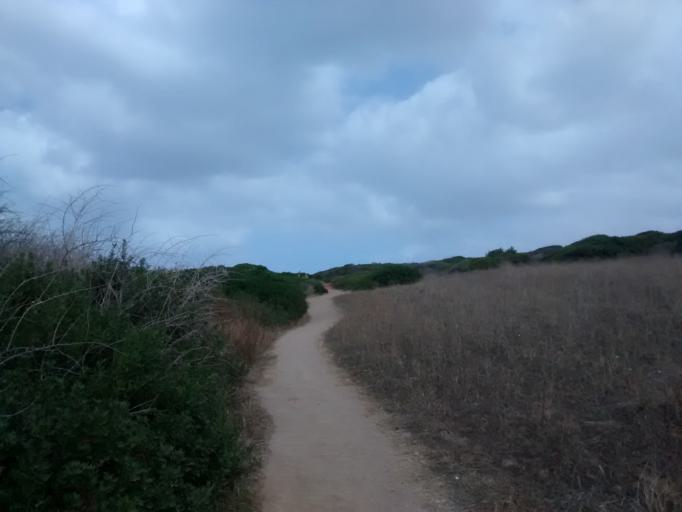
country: IT
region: Sardinia
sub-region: Provincia di Oristano
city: Narbolia
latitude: 40.0935
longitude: 8.4906
